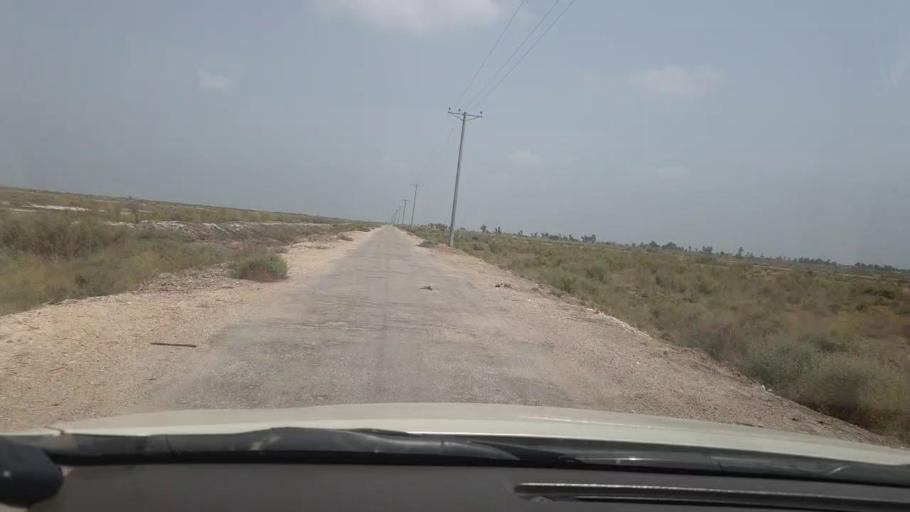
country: PK
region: Sindh
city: Garhi Yasin
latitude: 27.9880
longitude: 68.5017
